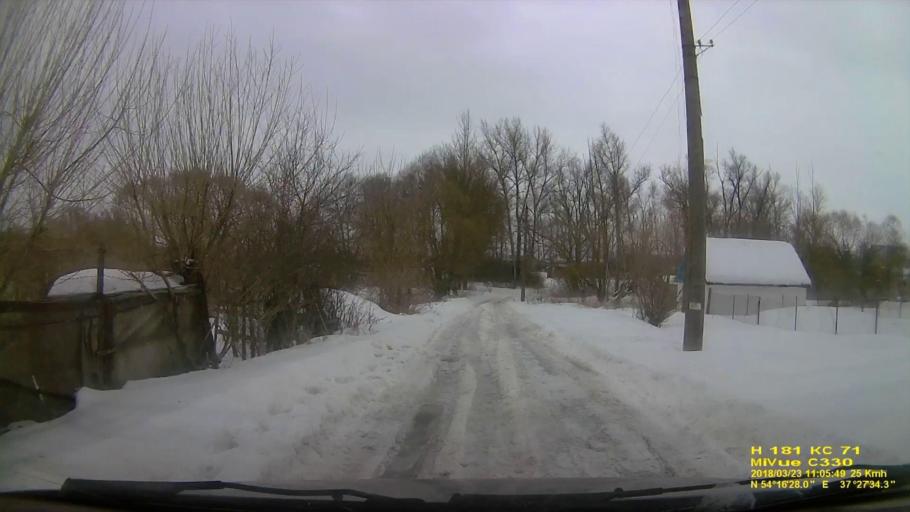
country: RU
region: Tula
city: Leninskiy
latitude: 54.2744
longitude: 37.4595
